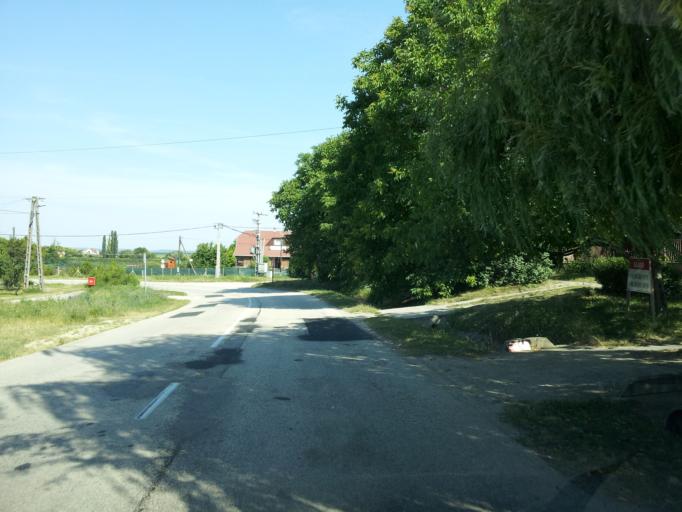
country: HU
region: Fejer
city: Lovasbereny
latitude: 47.3163
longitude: 18.5526
